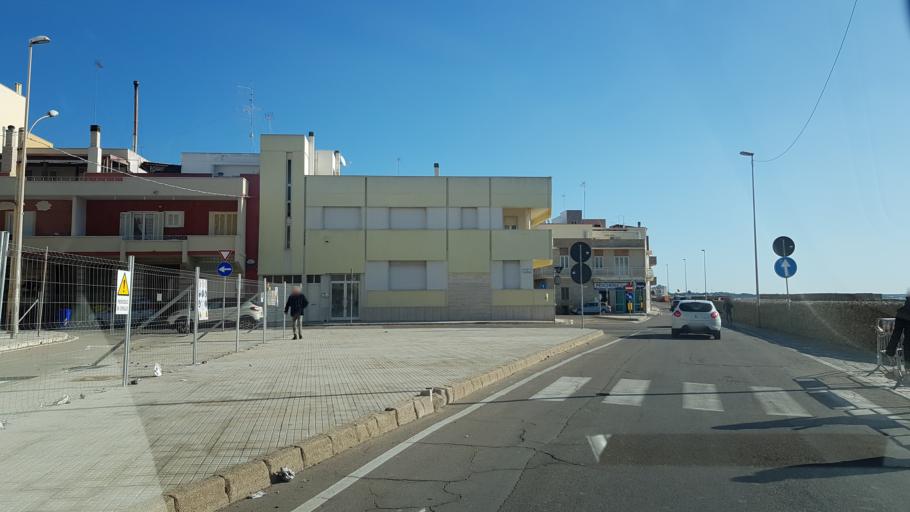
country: IT
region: Apulia
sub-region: Provincia di Lecce
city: Gallipoli
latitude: 40.0550
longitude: 17.9842
